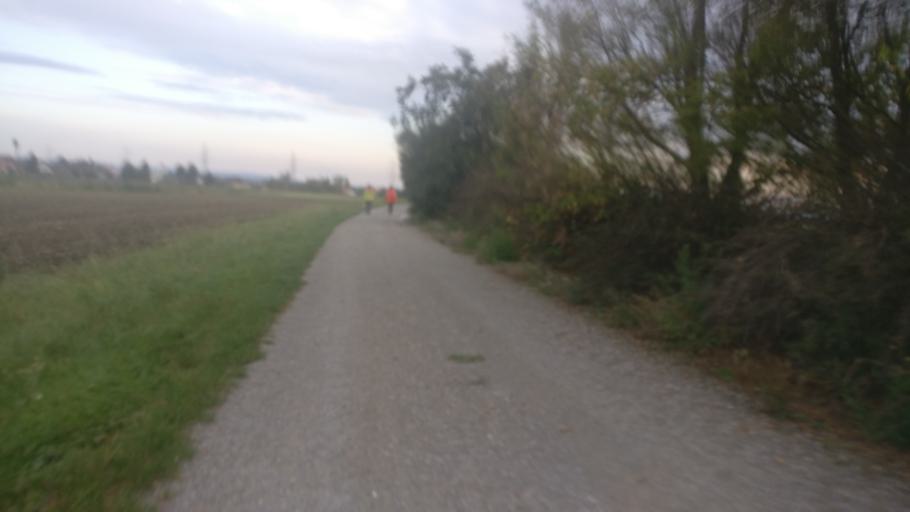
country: AT
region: Lower Austria
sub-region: Politischer Bezirk Wien-Umgebung
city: Lanzendorf
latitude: 48.1138
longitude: 16.4350
